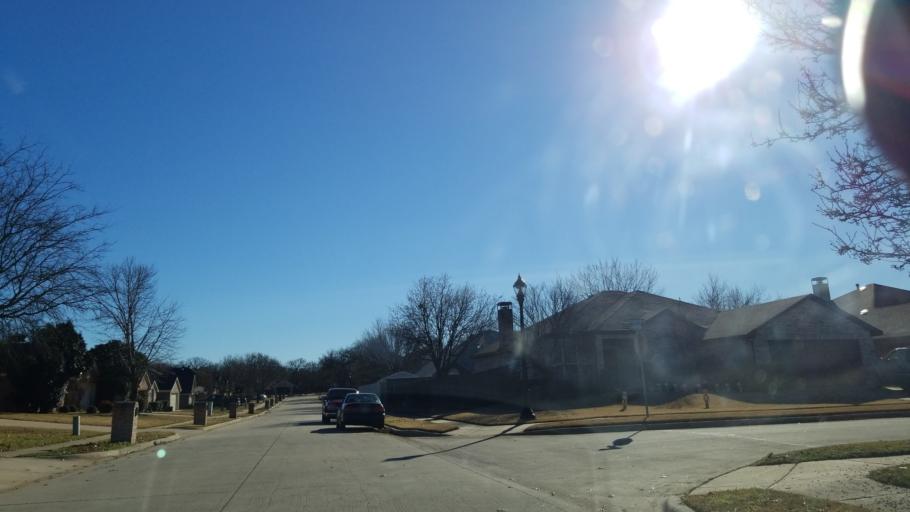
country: US
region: Texas
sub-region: Denton County
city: Corinth
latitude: 33.1401
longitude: -97.0815
